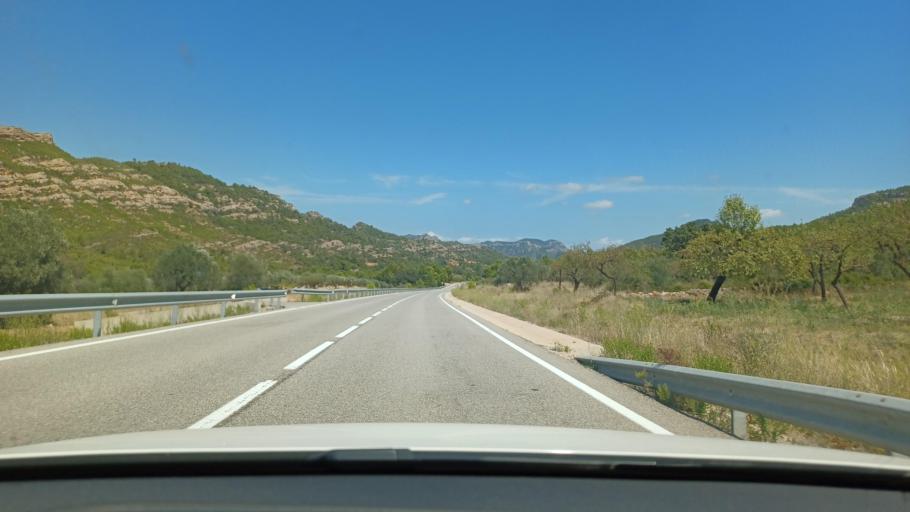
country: ES
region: Catalonia
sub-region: Provincia de Tarragona
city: Bot
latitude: 40.9722
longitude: 0.3836
